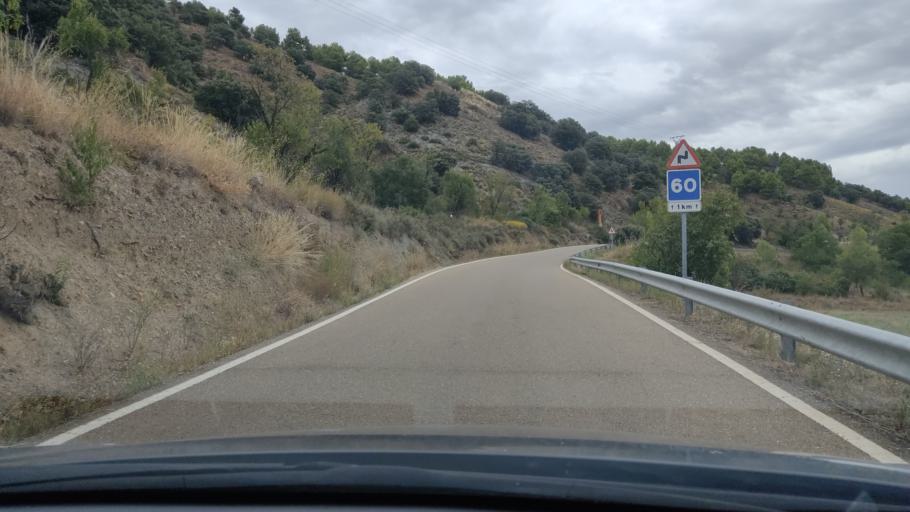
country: ES
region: Aragon
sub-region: Provincia de Zaragoza
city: Murero
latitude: 41.1581
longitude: -1.4801
